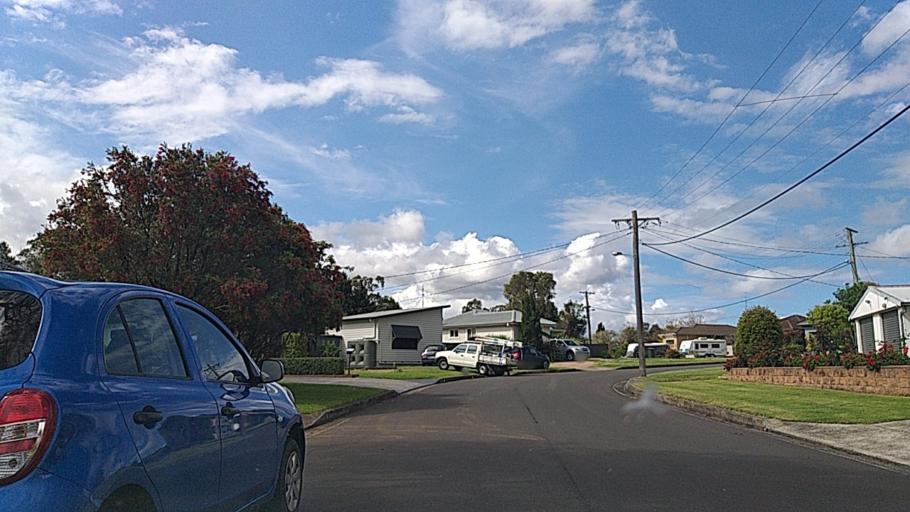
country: AU
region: New South Wales
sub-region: Wollongong
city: Koonawarra
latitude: -34.4908
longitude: 150.8059
